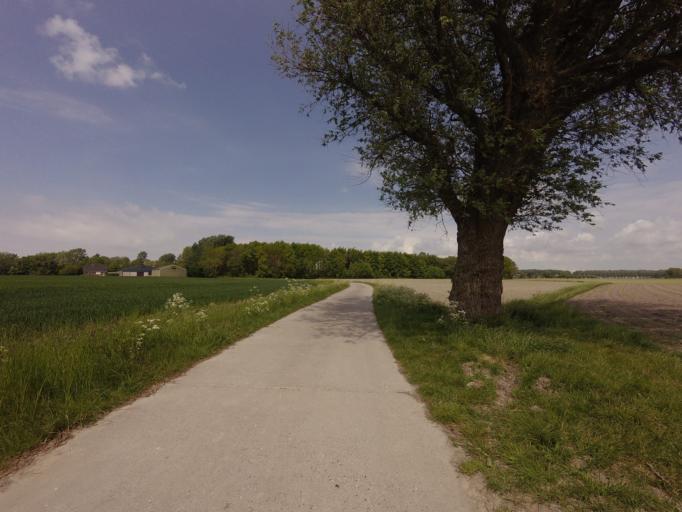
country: NL
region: Friesland
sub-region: Sudwest Fryslan
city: Bolsward
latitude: 53.1082
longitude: 5.4815
